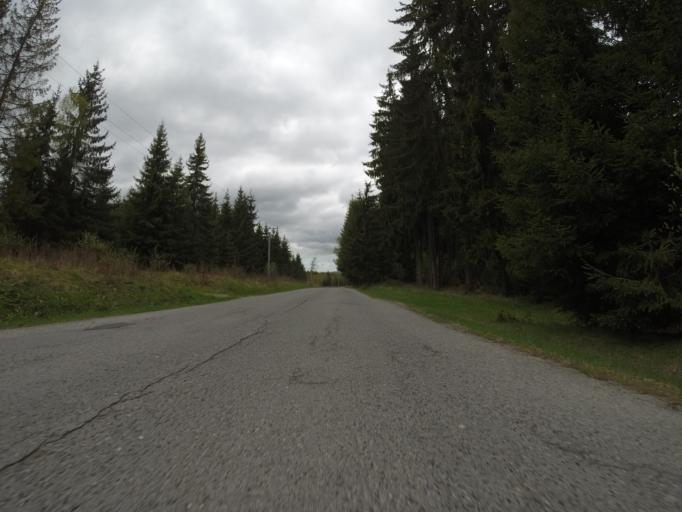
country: SK
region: Banskobystricky
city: Cierny Balog
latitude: 48.6430
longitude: 19.6392
